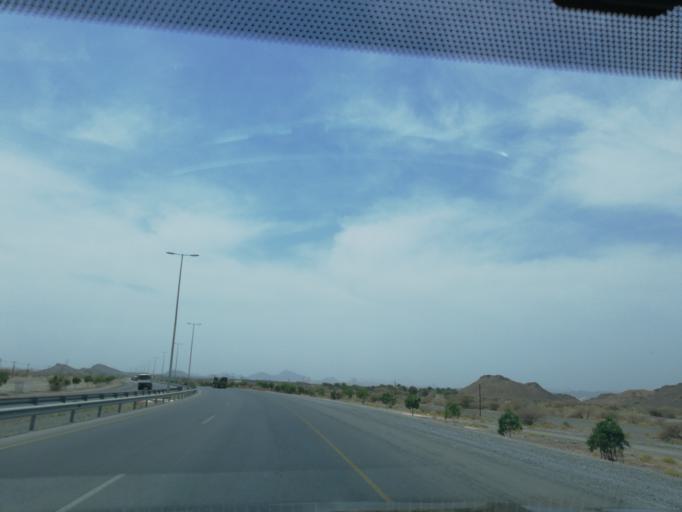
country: OM
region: Muhafazat ad Dakhiliyah
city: Nizwa
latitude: 22.8628
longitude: 57.5802
